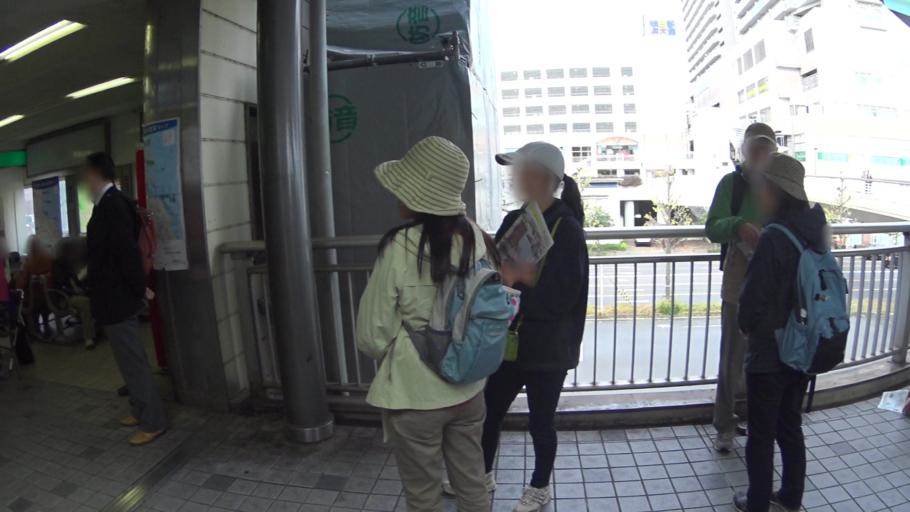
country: JP
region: Shiga Prefecture
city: Otsu-shi
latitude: 35.0095
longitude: 135.8619
